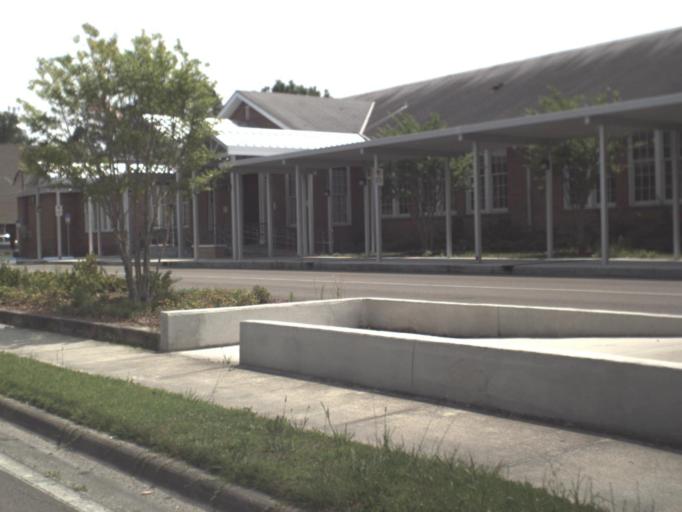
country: US
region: Florida
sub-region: Nassau County
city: Callahan
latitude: 30.5615
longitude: -81.8315
